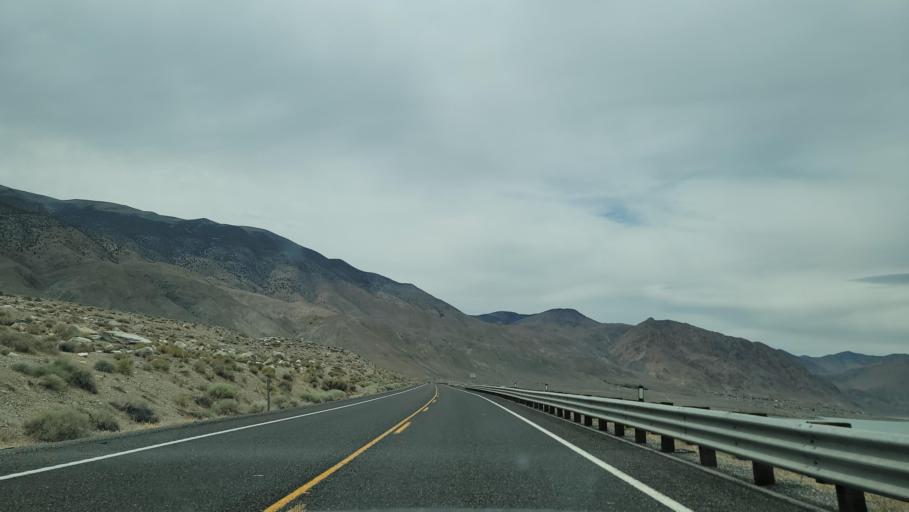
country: US
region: Nevada
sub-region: Mineral County
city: Hawthorne
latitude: 38.6128
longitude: -118.7206
